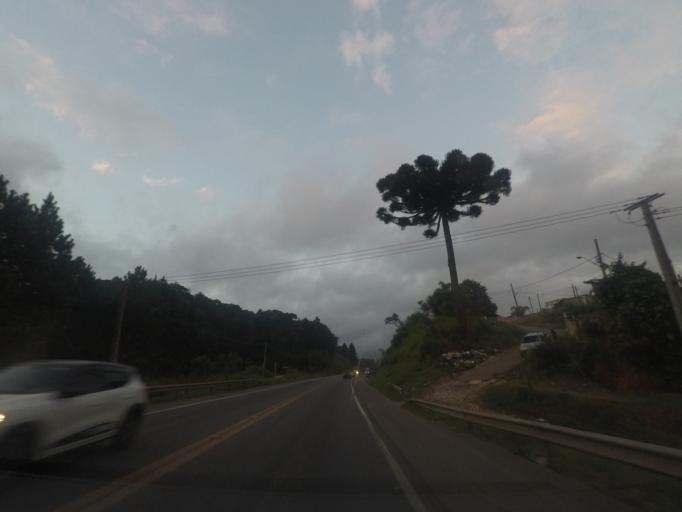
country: BR
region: Parana
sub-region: Almirante Tamandare
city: Almirante Tamandare
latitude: -25.3937
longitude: -49.3595
